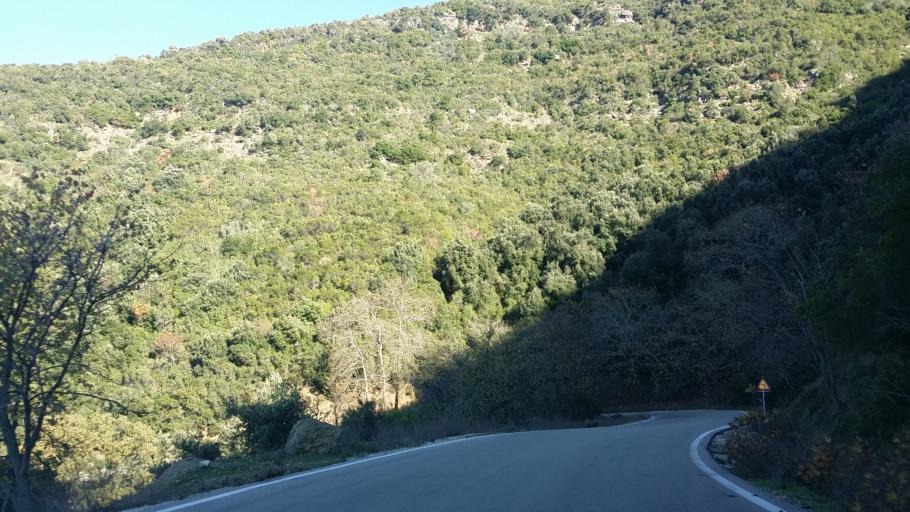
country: GR
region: West Greece
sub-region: Nomos Aitolias kai Akarnanias
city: Krikellos
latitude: 38.9644
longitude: 21.2350
